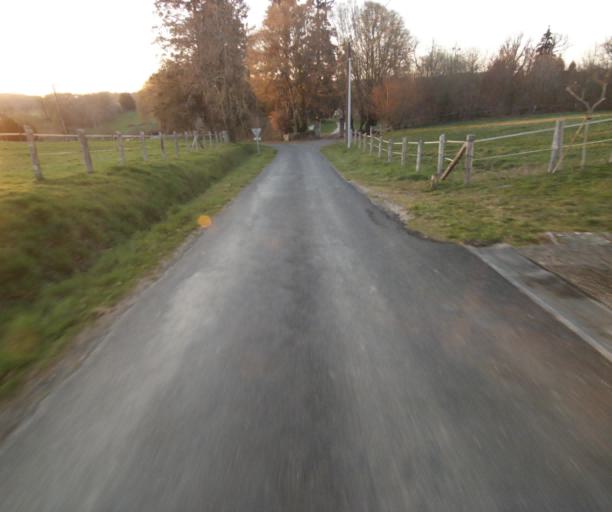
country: FR
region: Limousin
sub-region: Departement de la Correze
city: Saint-Clement
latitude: 45.3653
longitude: 1.6207
